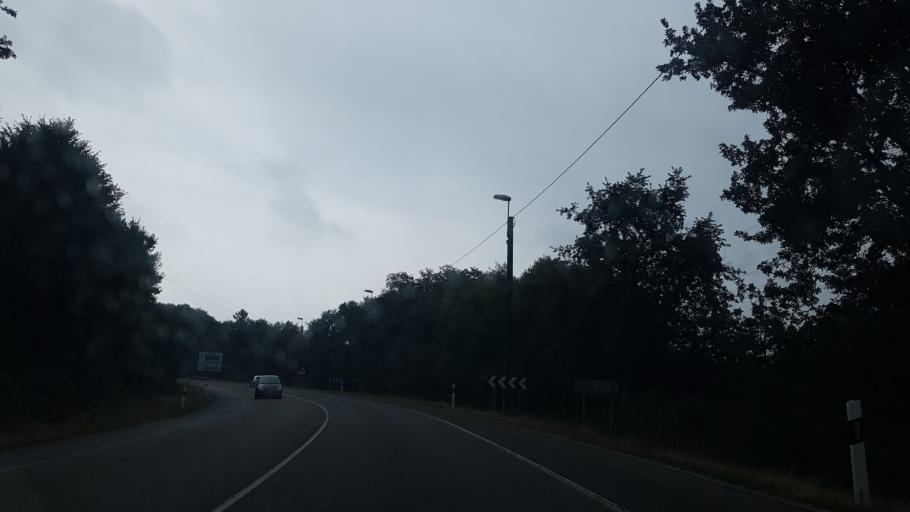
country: ES
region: Galicia
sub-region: Provincia de Lugo
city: Lugo
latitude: 42.9903
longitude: -7.5896
